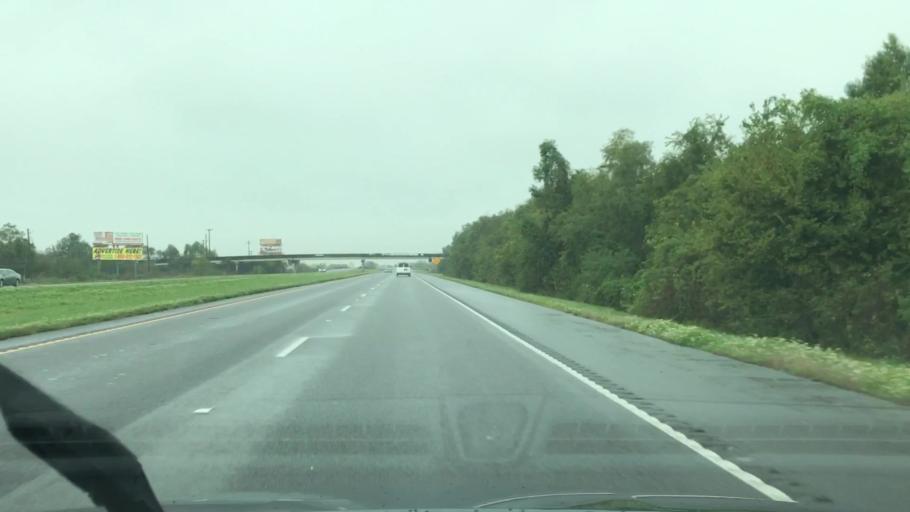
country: US
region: Louisiana
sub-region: Lafourche Parish
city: Raceland
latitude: 29.6904
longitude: -90.5990
